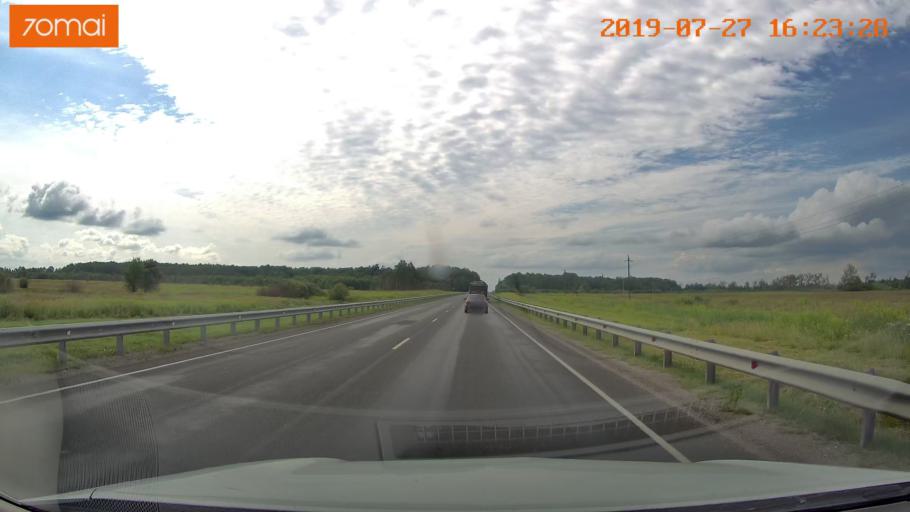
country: RU
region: Kaliningrad
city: Zheleznodorozhnyy
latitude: 54.6311
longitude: 21.4731
